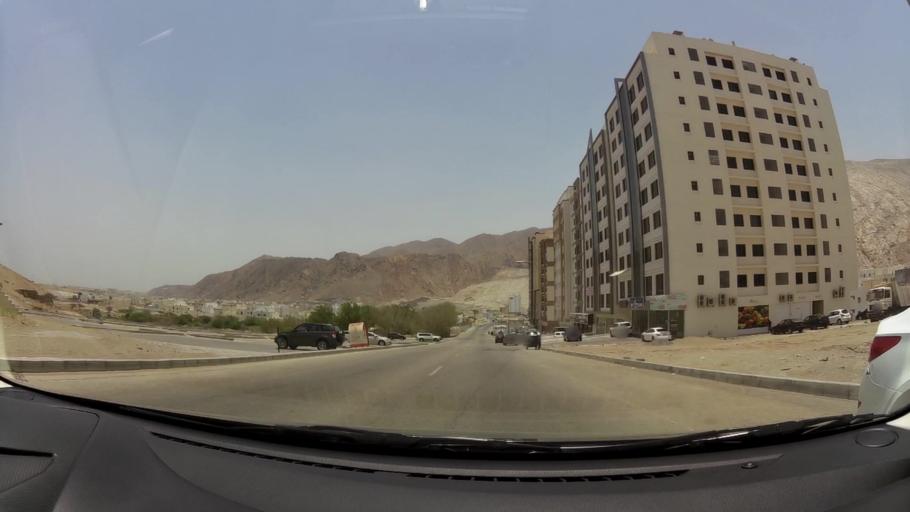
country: OM
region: Muhafazat Masqat
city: Bawshar
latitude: 23.5651
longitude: 58.4171
